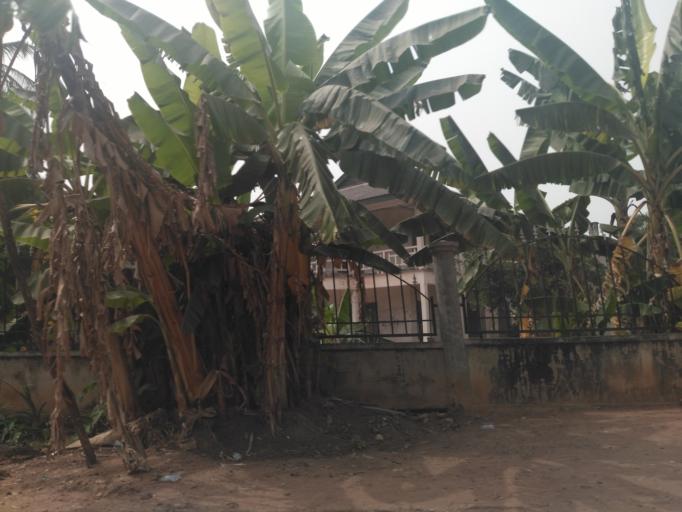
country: GH
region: Ashanti
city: Kumasi
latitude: 6.6749
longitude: -1.6190
